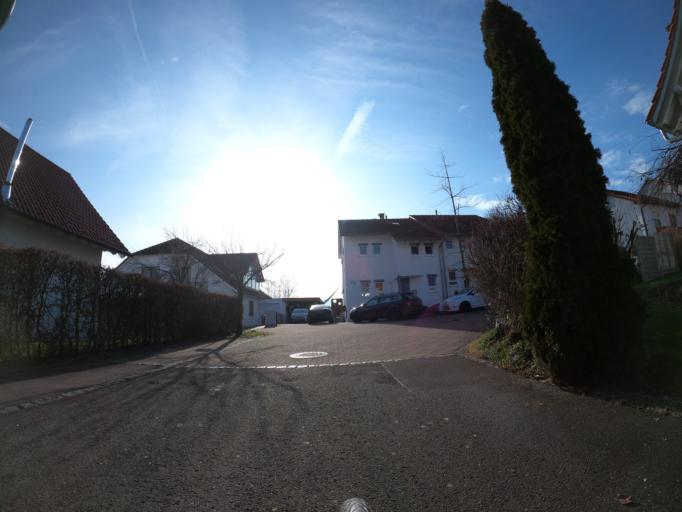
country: DE
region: Baden-Wuerttemberg
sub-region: Tuebingen Region
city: Metzingen
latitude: 48.5370
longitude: 9.2685
